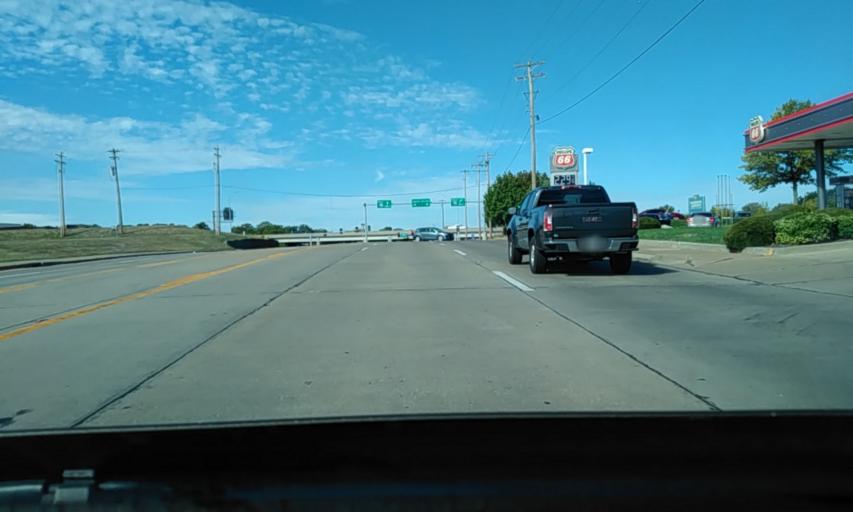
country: US
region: Missouri
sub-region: Saint Louis County
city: Mehlville
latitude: 38.4857
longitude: -90.3528
